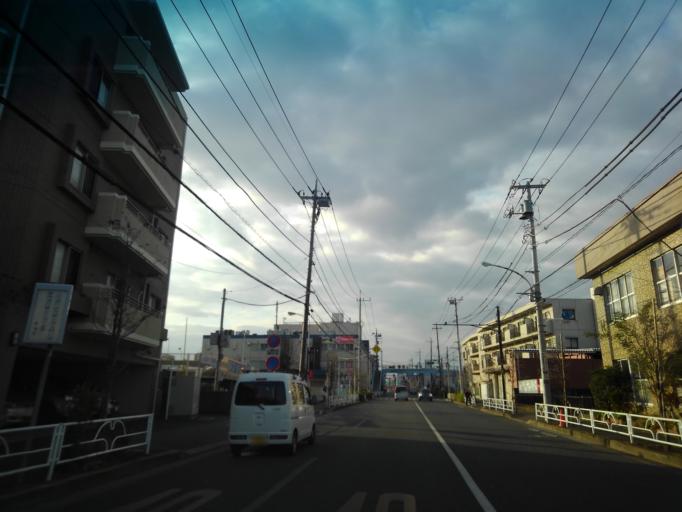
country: JP
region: Tokyo
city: Tanashicho
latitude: 35.7293
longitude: 139.5119
